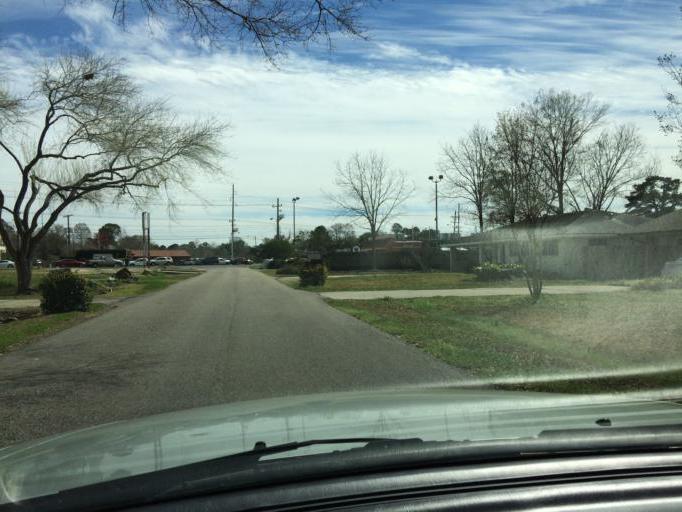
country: US
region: Louisiana
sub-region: Lafayette Parish
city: Lafayette
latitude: 30.1999
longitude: -92.0566
